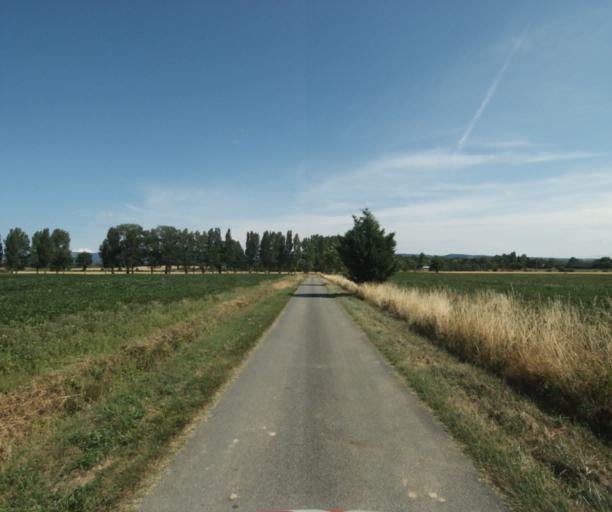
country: FR
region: Midi-Pyrenees
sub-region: Departement de la Haute-Garonne
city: Revel
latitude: 43.4926
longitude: 1.9889
